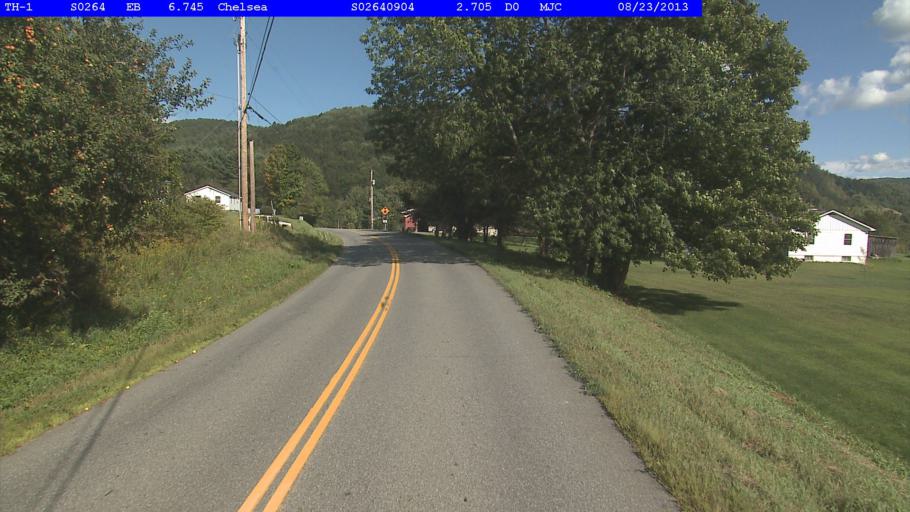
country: US
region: Vermont
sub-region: Orange County
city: Chelsea
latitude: 43.9620
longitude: -72.4677
